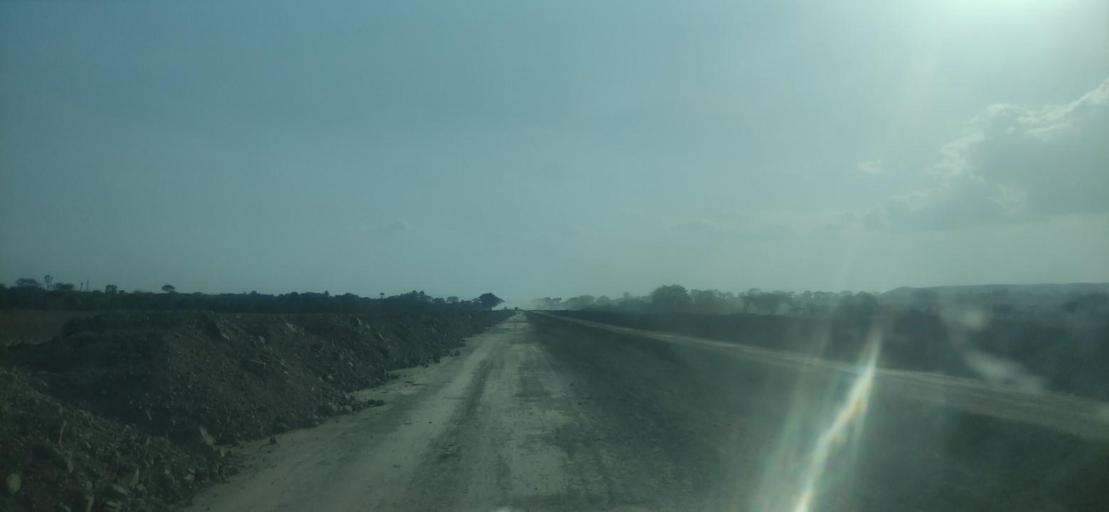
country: ET
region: Southern Nations, Nationalities, and People's Region
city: Hawassa
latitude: 7.1622
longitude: 38.4839
